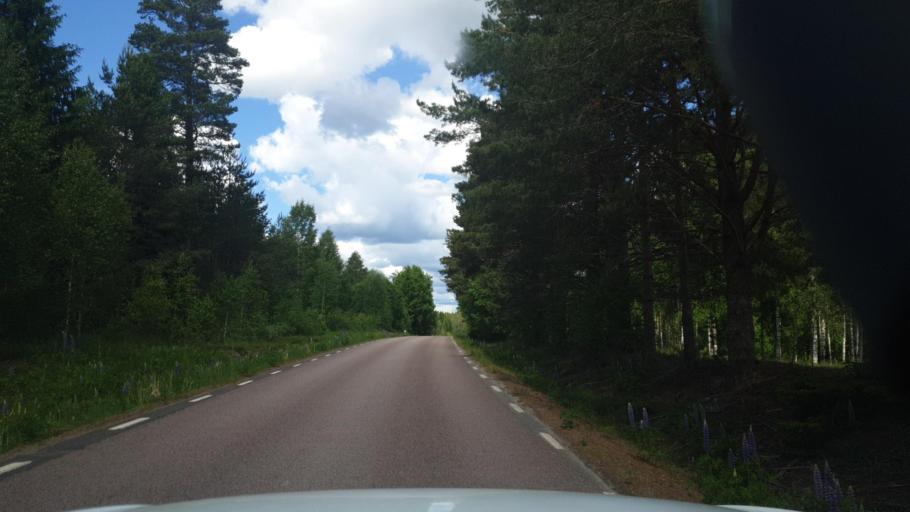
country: SE
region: Vaermland
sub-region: Karlstads Kommun
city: Edsvalla
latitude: 59.5143
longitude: 13.1103
